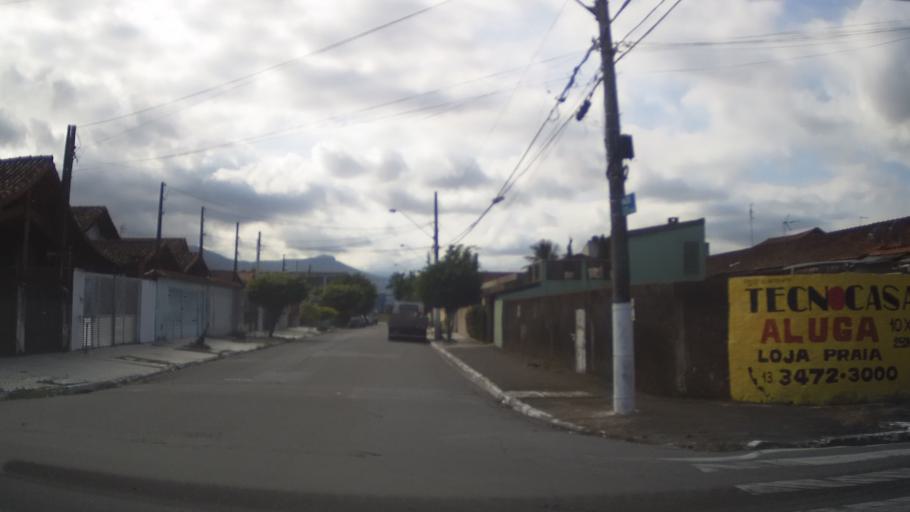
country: BR
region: Sao Paulo
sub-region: Praia Grande
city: Praia Grande
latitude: -24.0163
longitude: -46.4566
